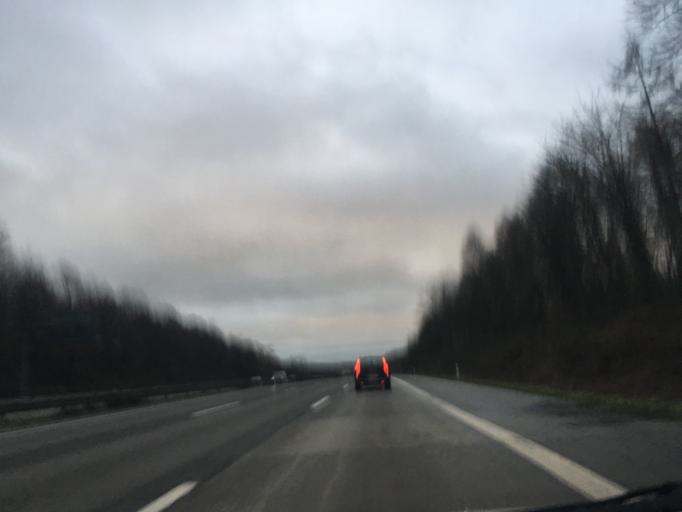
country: DE
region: North Rhine-Westphalia
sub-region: Regierungsbezirk Dusseldorf
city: Ratingen
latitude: 51.3316
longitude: 6.8828
